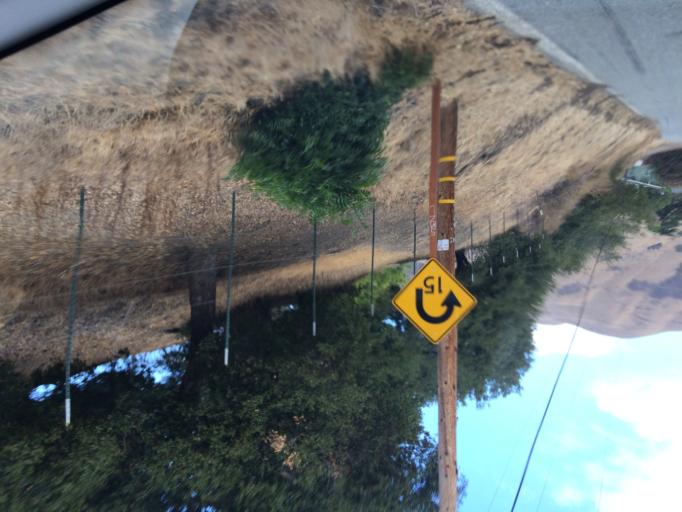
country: US
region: California
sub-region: Santa Clara County
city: East Foothills
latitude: 37.3899
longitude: -121.8029
